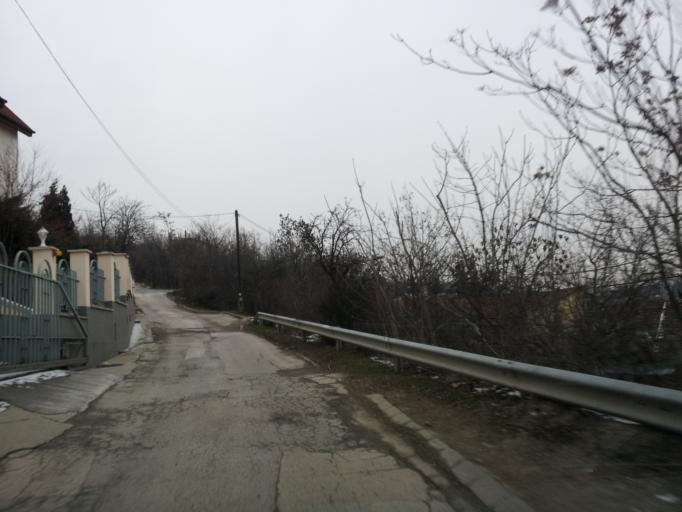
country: HU
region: Budapest
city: Budapest XII. keruelet
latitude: 47.4899
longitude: 18.9920
